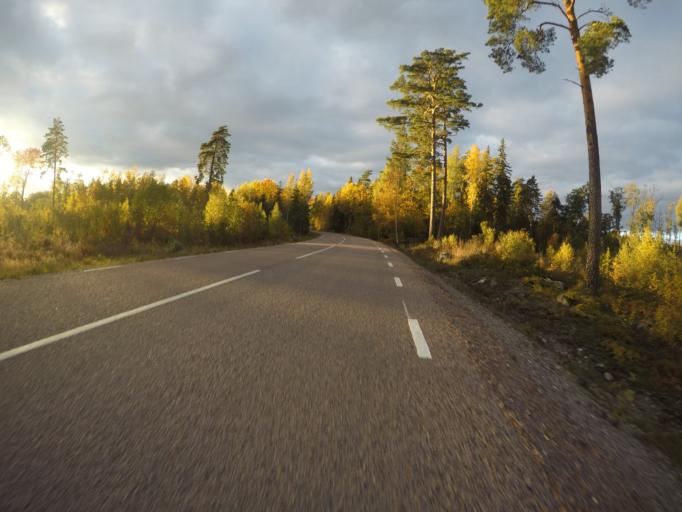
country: SE
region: Vaestmanland
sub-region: Arboga Kommun
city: Tyringe
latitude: 59.3068
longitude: 16.0005
